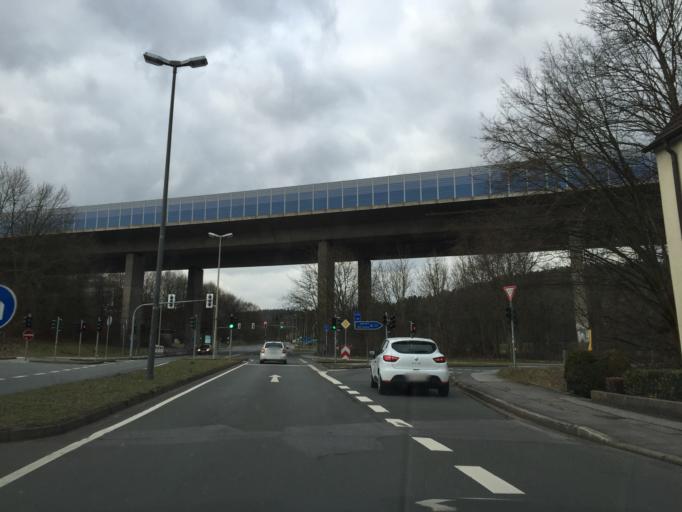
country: DE
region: North Rhine-Westphalia
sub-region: Regierungsbezirk Arnsberg
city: Nachrodt-Wiblingwerde
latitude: 51.3718
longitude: 7.6116
